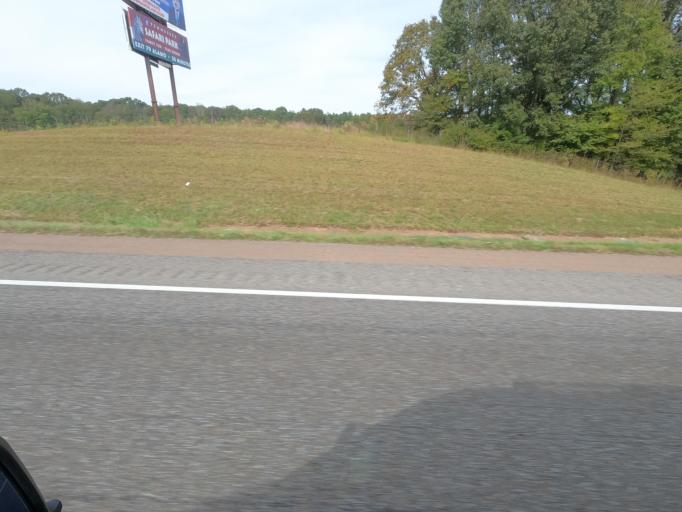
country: US
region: Tennessee
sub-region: Henderson County
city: Lexington
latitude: 35.7844
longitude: -88.4077
